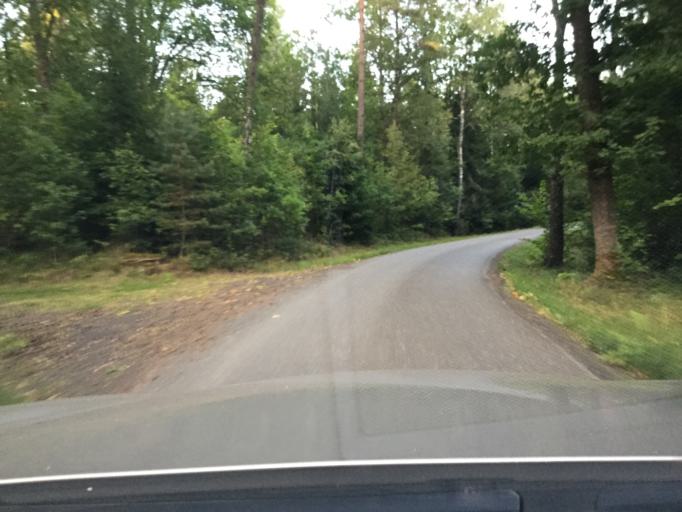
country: SE
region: Kronoberg
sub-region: Almhults Kommun
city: AElmhult
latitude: 56.6119
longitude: 14.2220
